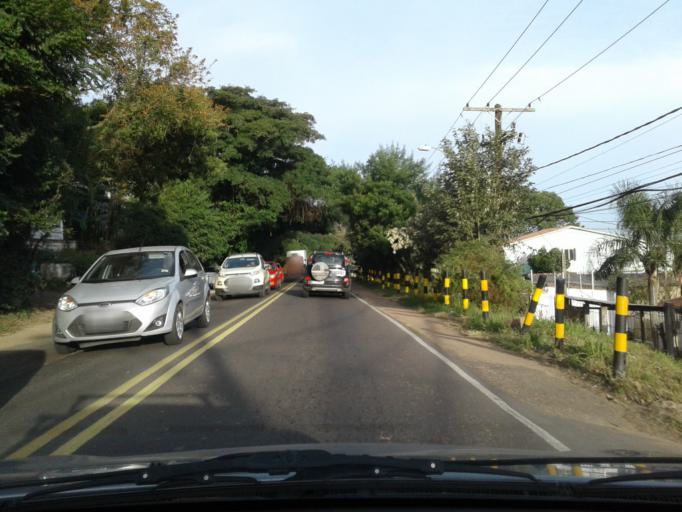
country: BR
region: Rio Grande do Sul
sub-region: Porto Alegre
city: Porto Alegre
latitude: -30.1079
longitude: -51.2214
